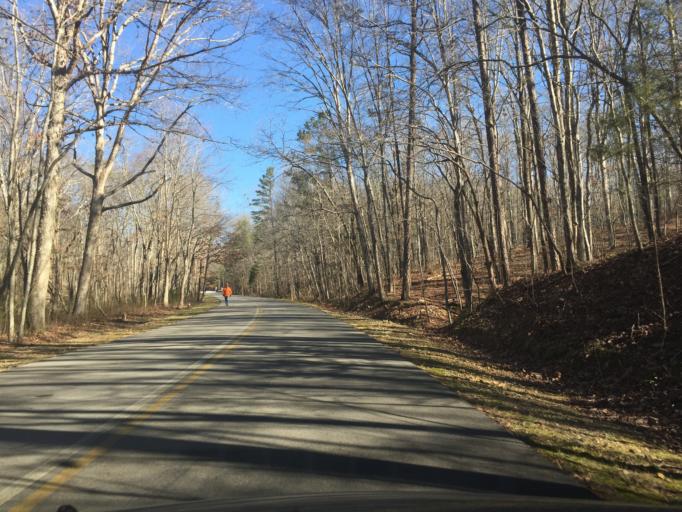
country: US
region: Tennessee
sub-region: Hamilton County
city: Harrison
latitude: 35.0824
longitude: -85.1178
